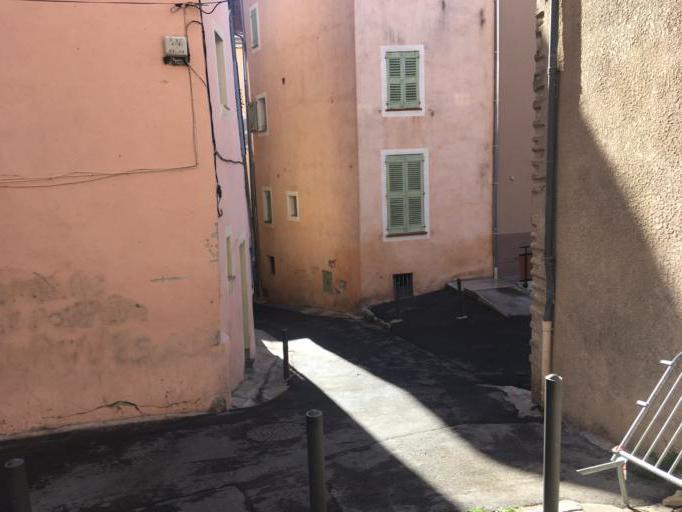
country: FR
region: Provence-Alpes-Cote d'Azur
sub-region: Departement du Var
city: Draguignan
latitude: 43.5393
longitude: 6.4668
